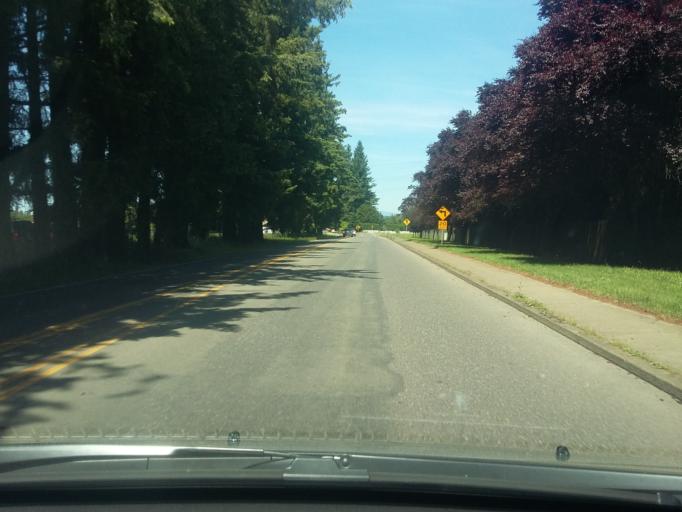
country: US
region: Washington
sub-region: Clark County
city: Mill Plain
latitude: 45.6337
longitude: -122.4759
